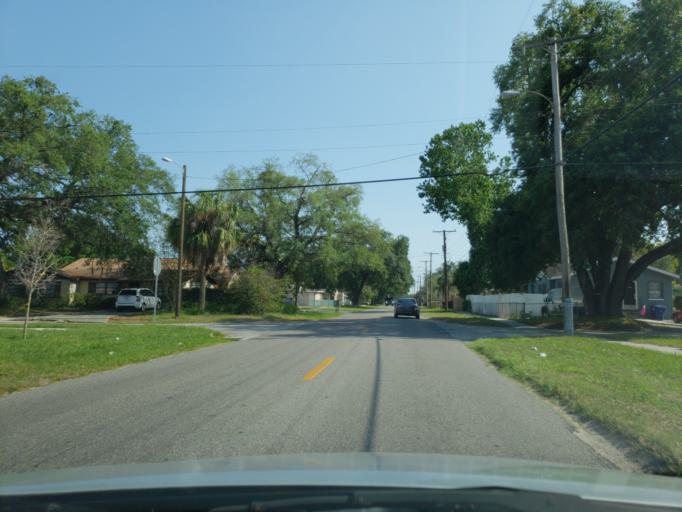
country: US
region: Florida
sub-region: Hillsborough County
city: Tampa
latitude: 27.9721
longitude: -82.4931
